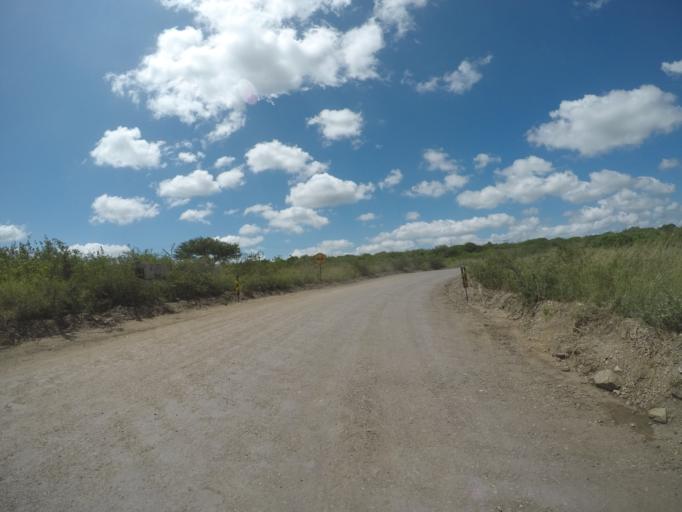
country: ZA
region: KwaZulu-Natal
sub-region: uThungulu District Municipality
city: Empangeni
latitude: -28.6605
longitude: 31.7810
